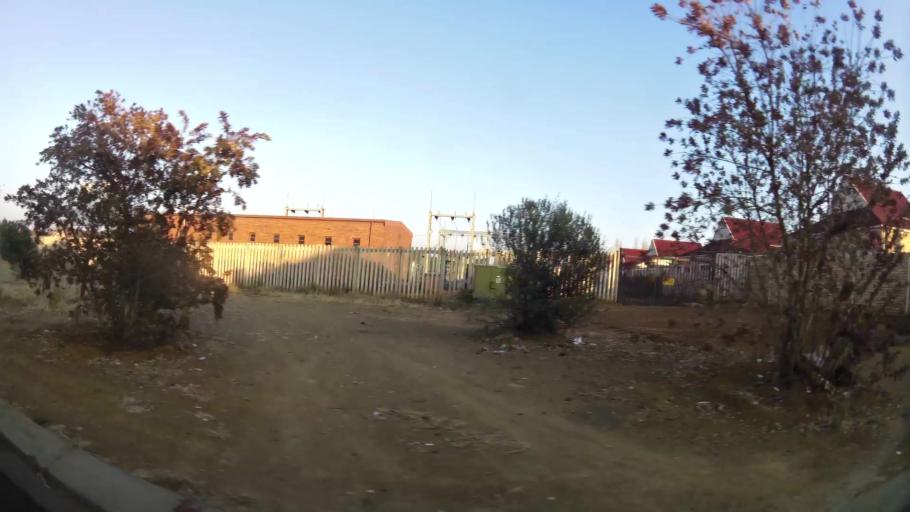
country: ZA
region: Orange Free State
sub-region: Mangaung Metropolitan Municipality
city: Bloemfontein
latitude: -29.1041
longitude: 26.1637
